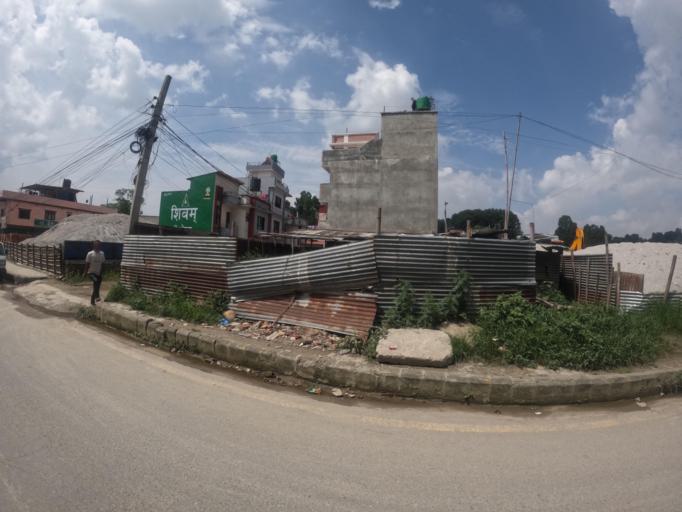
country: NP
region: Central Region
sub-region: Bagmati Zone
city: Bhaktapur
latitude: 27.6796
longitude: 85.3835
